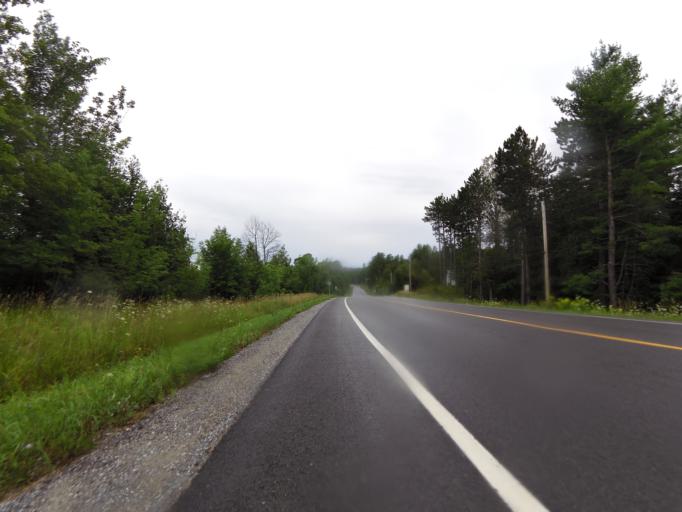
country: CA
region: Ontario
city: Perth
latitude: 45.0114
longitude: -76.3686
